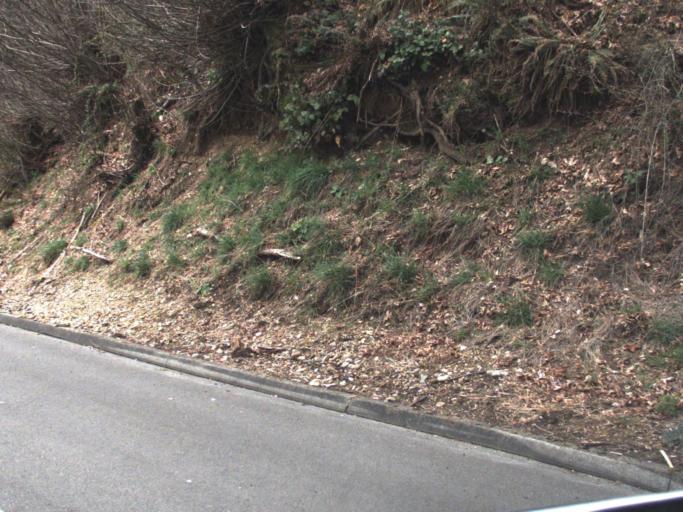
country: US
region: Washington
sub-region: King County
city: Kent
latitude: 47.3854
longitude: -122.2775
